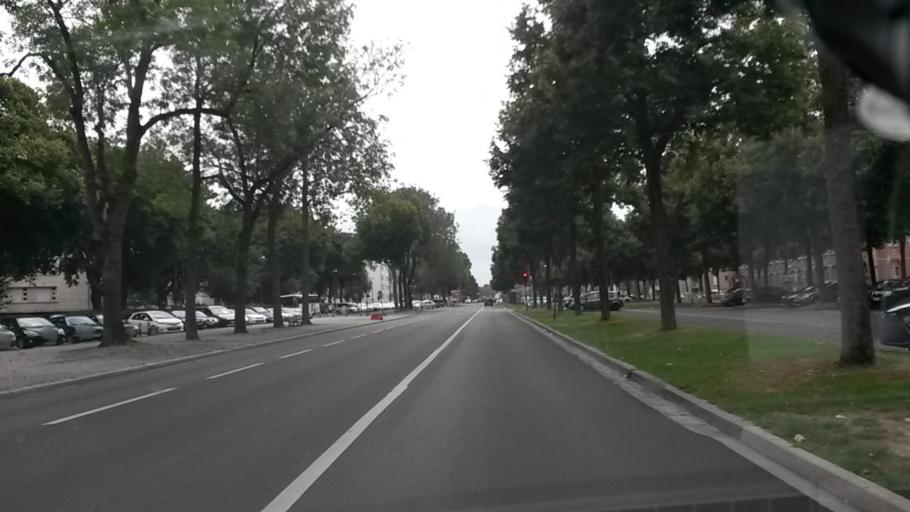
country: FR
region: Picardie
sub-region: Departement de la Somme
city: Amiens
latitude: 49.8956
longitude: 2.2881
